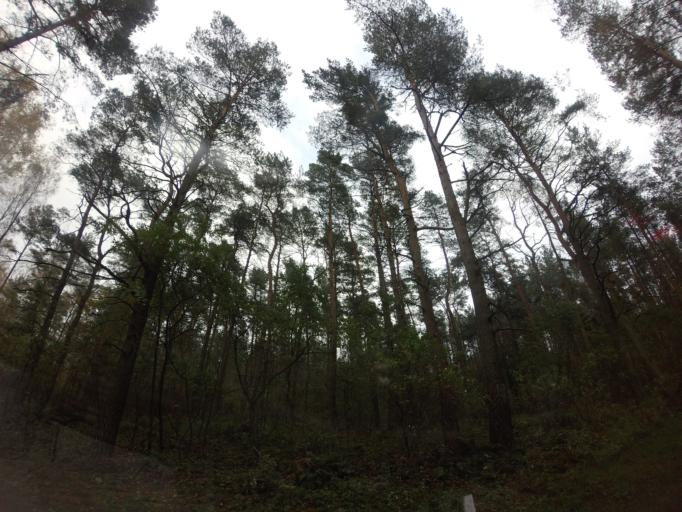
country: PL
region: West Pomeranian Voivodeship
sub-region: Powiat choszczenski
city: Bierzwnik
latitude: 53.1395
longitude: 15.6140
